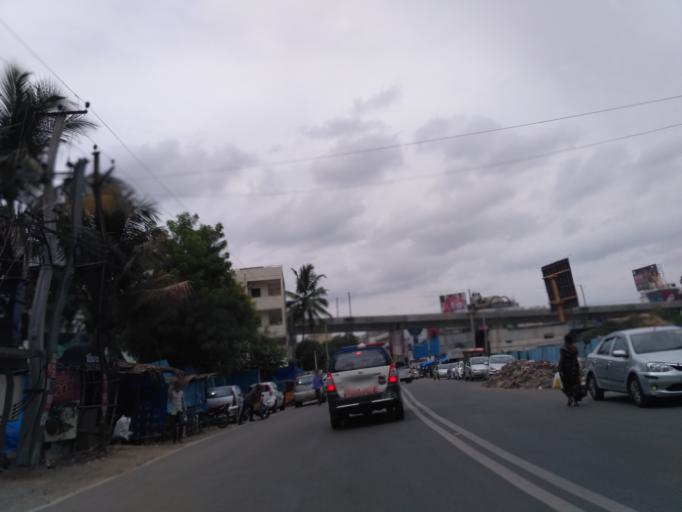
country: IN
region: Telangana
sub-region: Rangareddi
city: Kukatpalli
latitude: 17.4399
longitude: 78.3894
